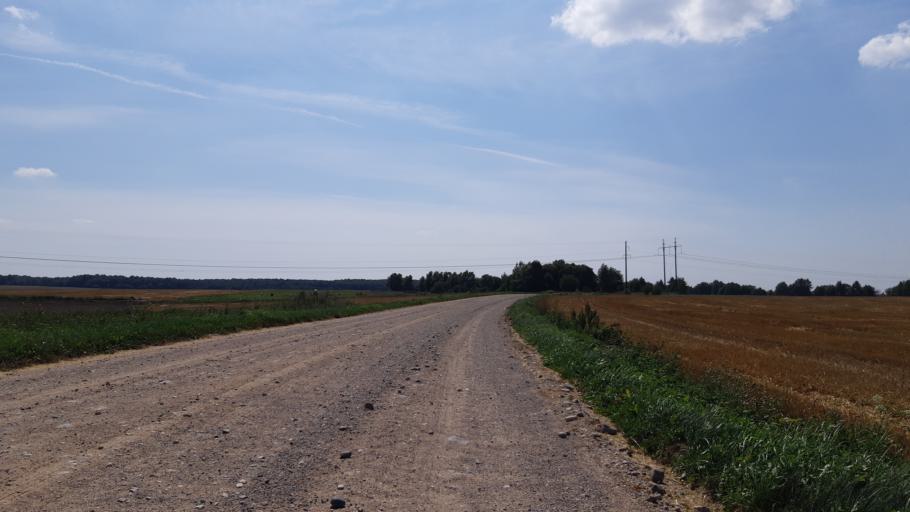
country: LT
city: Virbalis
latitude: 54.6212
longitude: 22.8075
